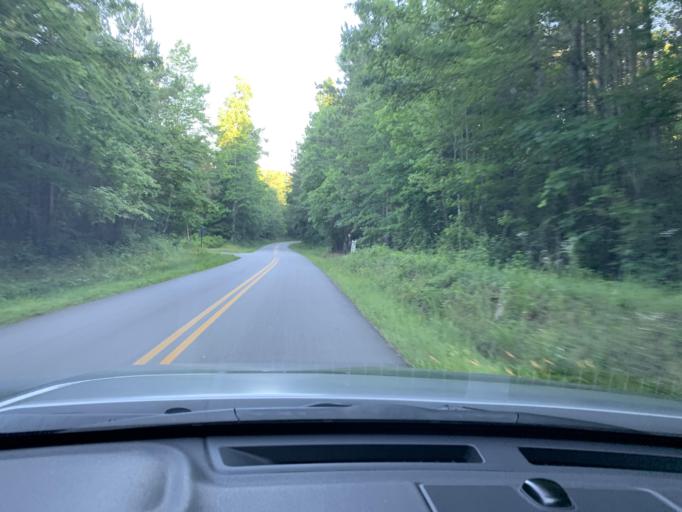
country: US
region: Georgia
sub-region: Bartow County
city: Rydal
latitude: 34.2646
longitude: -84.7077
